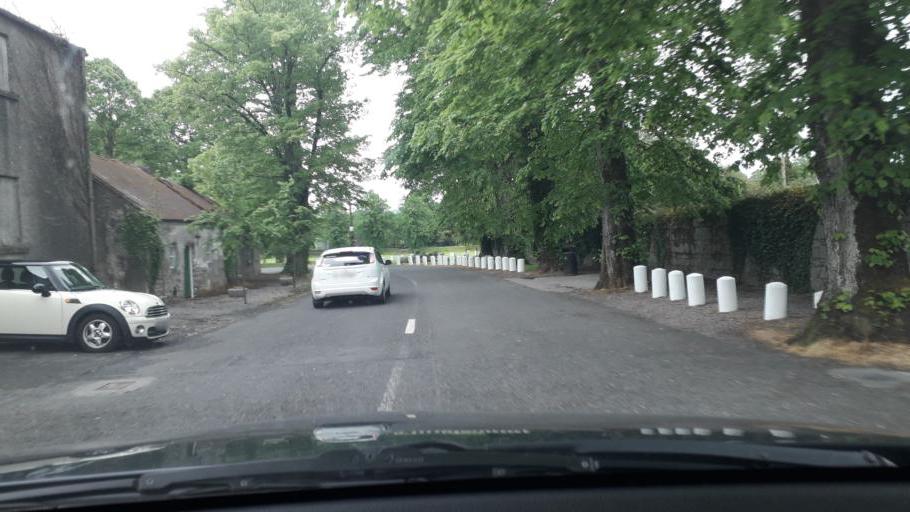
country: IE
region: Leinster
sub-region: Kildare
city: Castledermot
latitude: 52.9121
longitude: -6.8365
